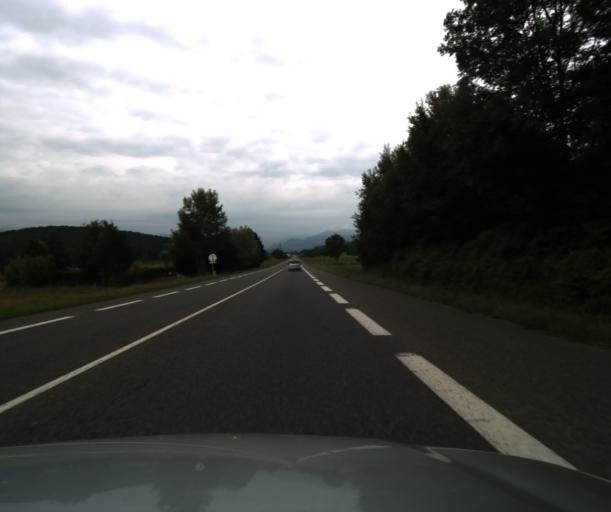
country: FR
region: Midi-Pyrenees
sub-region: Departement des Hautes-Pyrenees
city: Ossun
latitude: 43.1551
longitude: -0.0207
